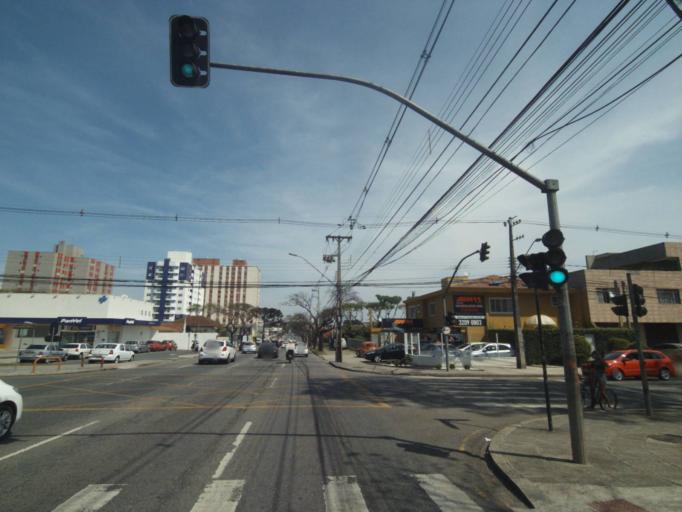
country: BR
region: Parana
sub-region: Curitiba
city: Curitiba
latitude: -25.4756
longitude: -49.2958
